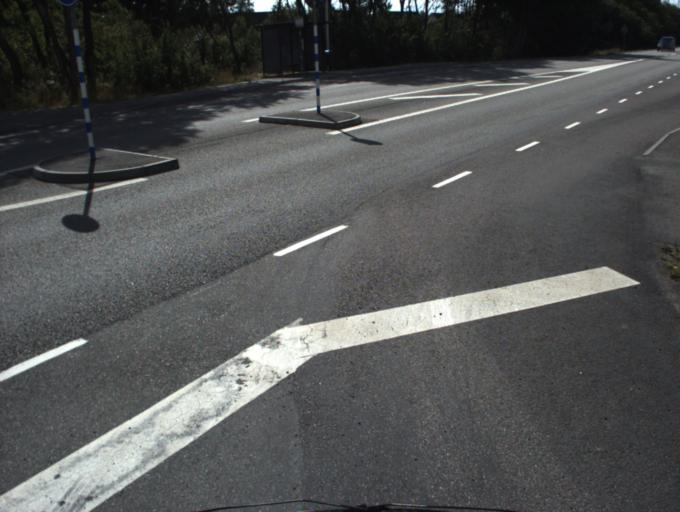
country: SE
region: Skane
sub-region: Helsingborg
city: Barslov
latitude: 56.0140
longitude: 12.7945
